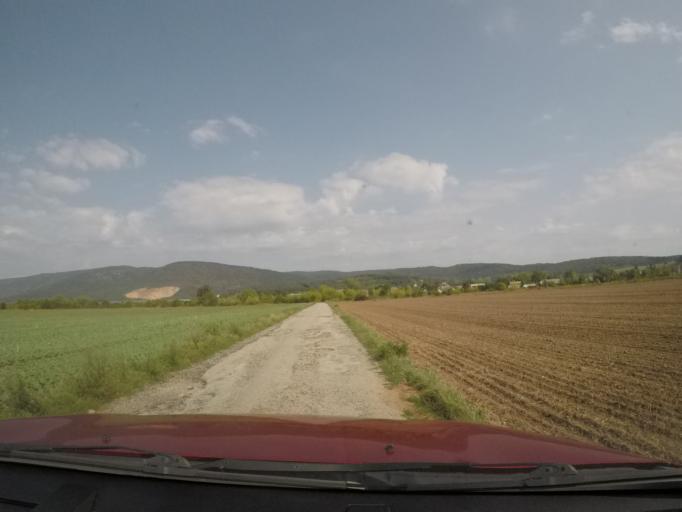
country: SK
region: Kosicky
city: Moldava nad Bodvou
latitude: 48.6039
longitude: 20.9525
